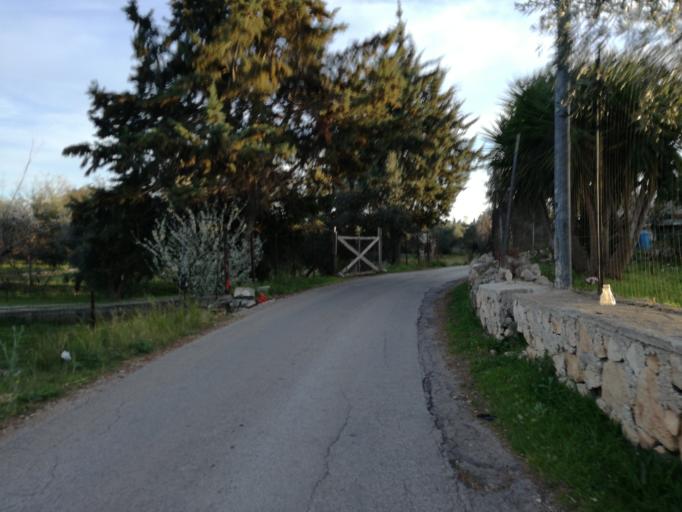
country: IT
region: Apulia
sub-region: Provincia di Bari
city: Lamie
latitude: 41.0355
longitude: 16.8806
